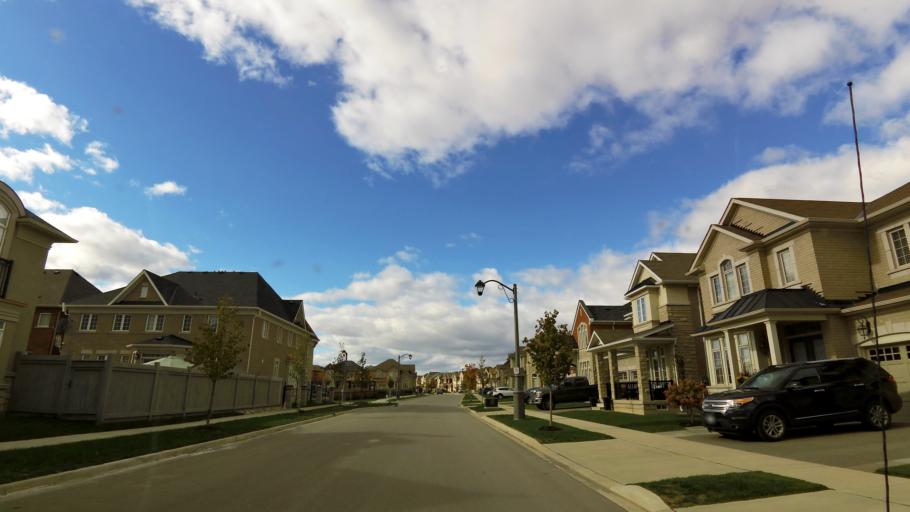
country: CA
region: Ontario
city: Oakville
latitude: 43.4702
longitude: -79.7470
